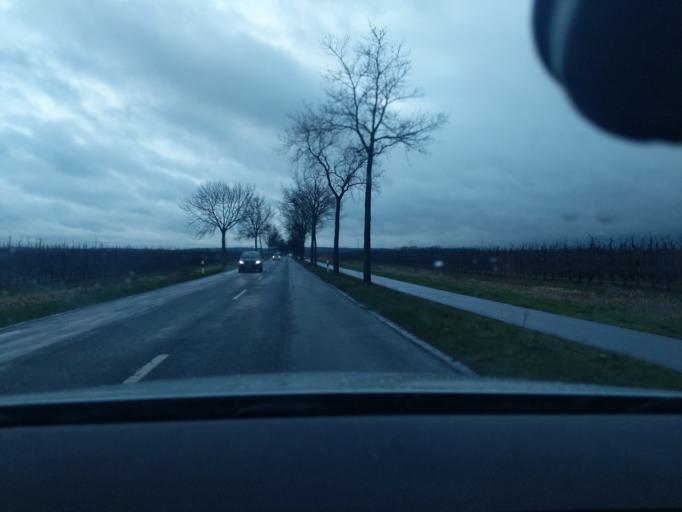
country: DE
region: Lower Saxony
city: Jork
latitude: 53.5151
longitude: 9.6690
